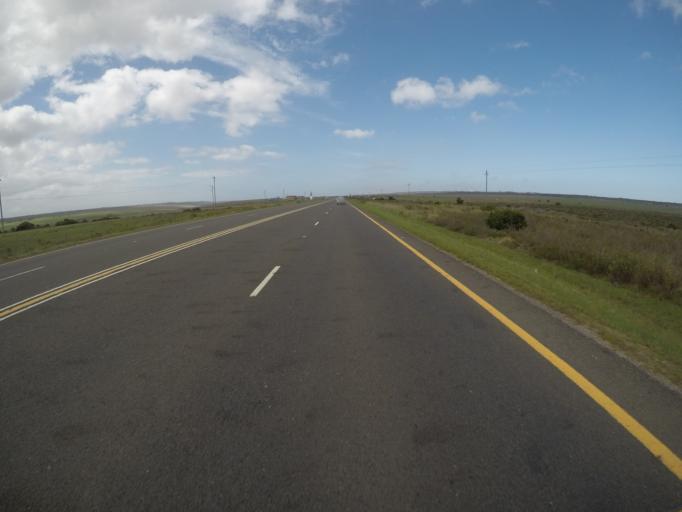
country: ZA
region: Western Cape
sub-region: Eden District Municipality
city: Mossel Bay
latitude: -34.1808
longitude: 22.0219
